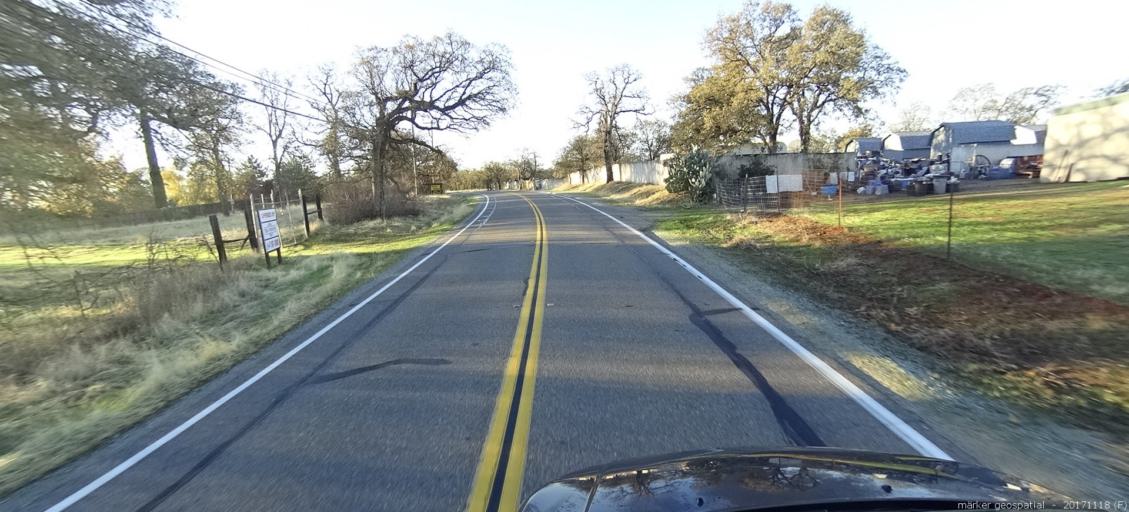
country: US
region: California
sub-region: Shasta County
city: Anderson
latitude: 40.4219
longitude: -122.2857
